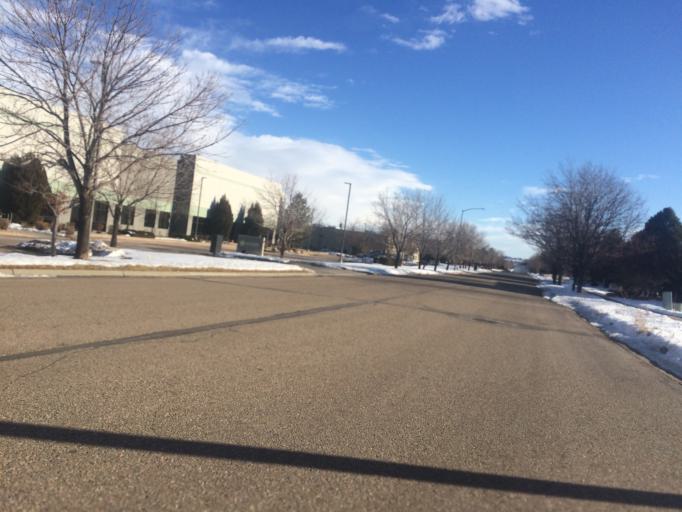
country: US
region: Colorado
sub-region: Boulder County
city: Louisville
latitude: 39.9668
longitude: -105.1253
